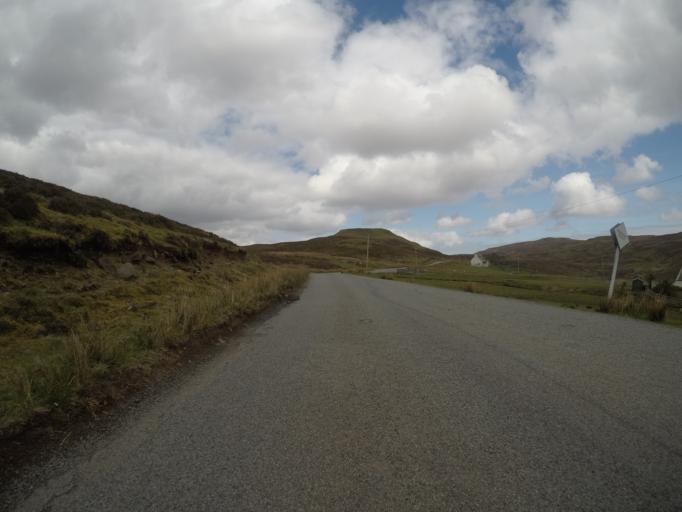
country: GB
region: Scotland
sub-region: Highland
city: Isle of Skye
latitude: 57.3740
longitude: -6.3763
